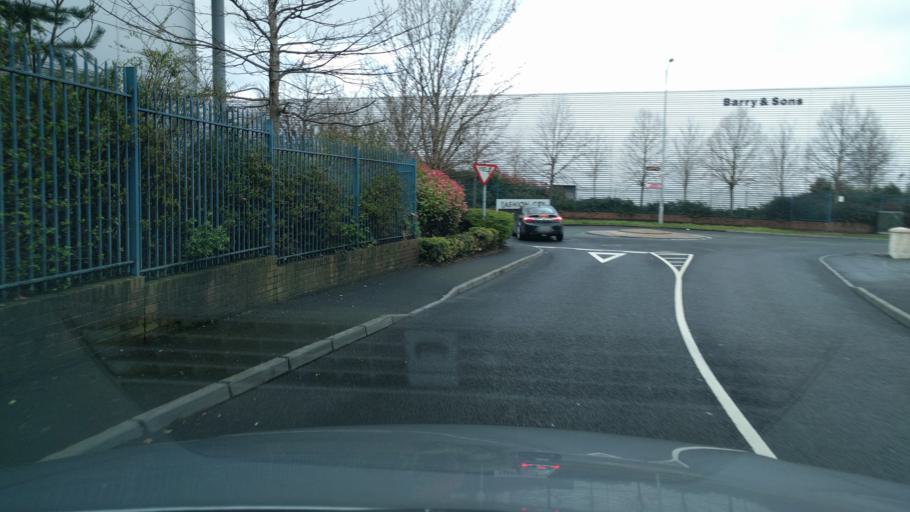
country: IE
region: Leinster
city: Firhouse
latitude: 53.3066
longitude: -6.3494
